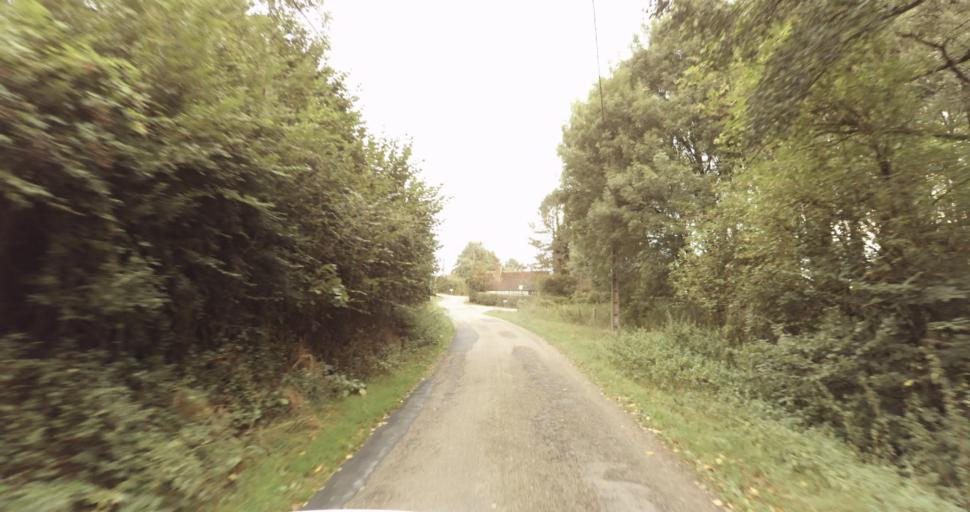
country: FR
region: Lower Normandy
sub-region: Departement de l'Orne
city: Trun
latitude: 48.9251
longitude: 0.0870
